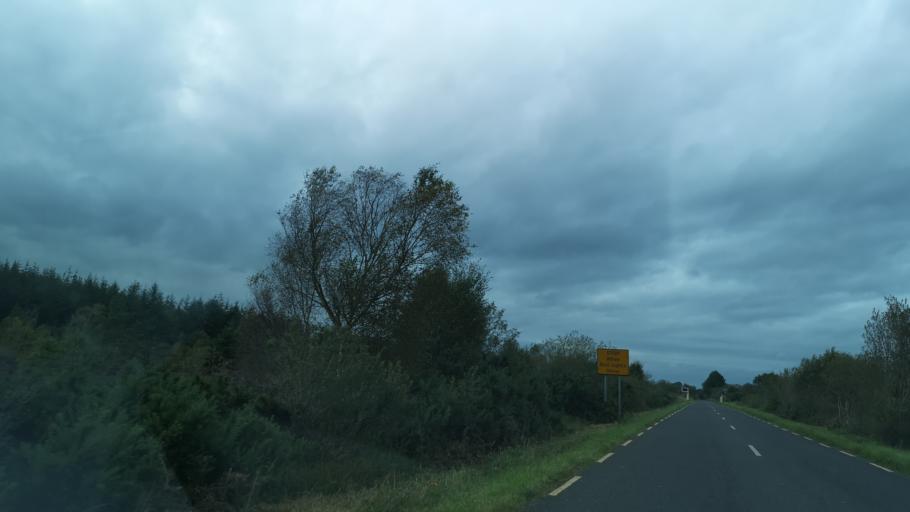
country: IE
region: Leinster
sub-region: Uibh Fhaili
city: Ferbane
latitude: 53.2091
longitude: -7.7871
